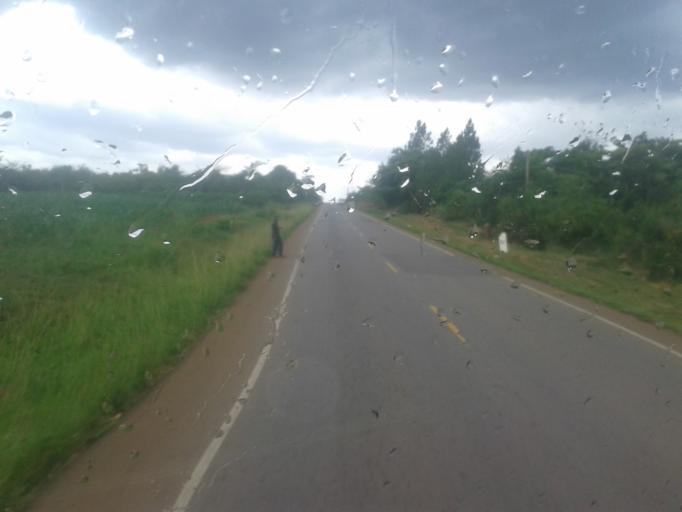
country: UG
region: Central Region
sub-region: Nakasongola District
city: Nakasongola
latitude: 1.3124
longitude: 32.4220
